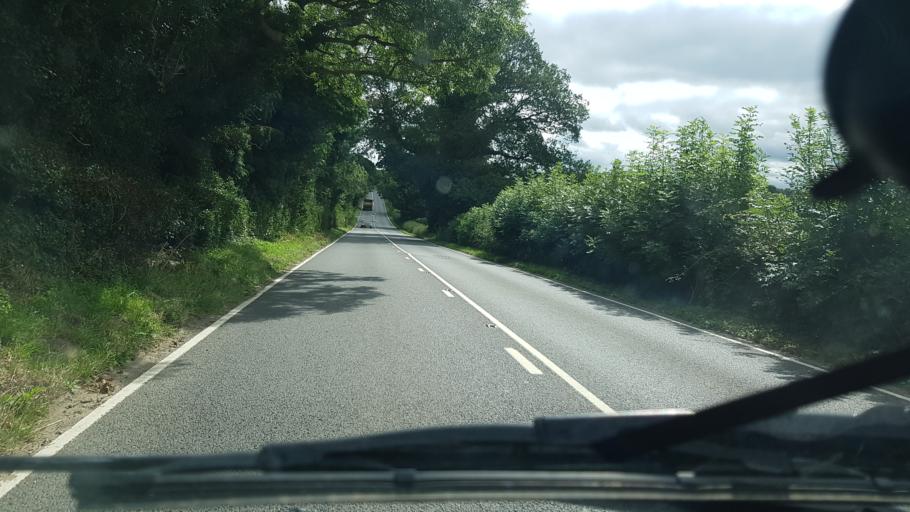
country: GB
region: England
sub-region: Surrey
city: Cranleigh
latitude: 51.0994
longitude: -0.4980
